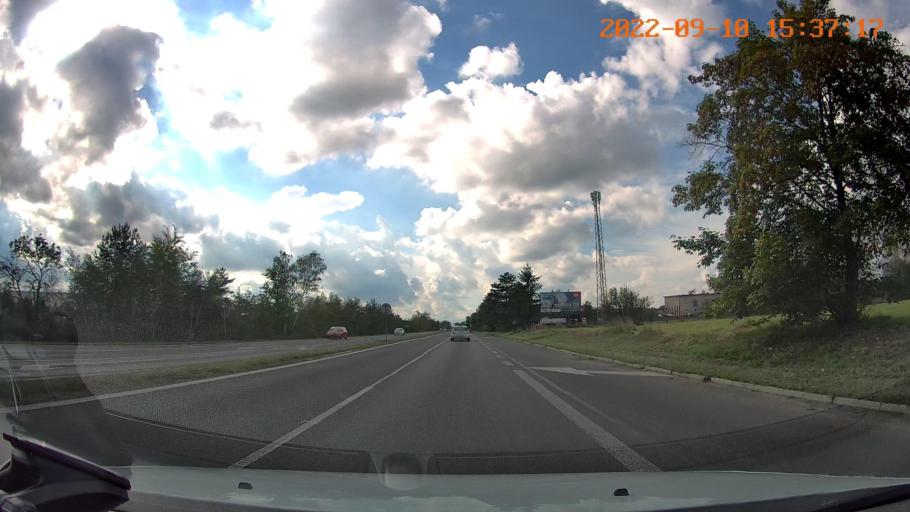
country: PL
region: Silesian Voivodeship
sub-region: Powiat bierunsko-ledzinski
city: Bierun
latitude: 50.1093
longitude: 19.0691
